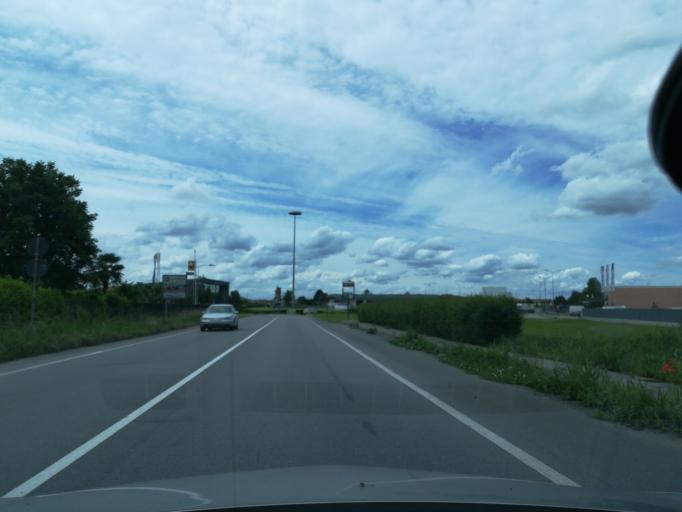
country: IT
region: Lombardy
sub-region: Provincia di Bergamo
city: Antegnate
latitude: 45.4894
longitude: 9.7989
